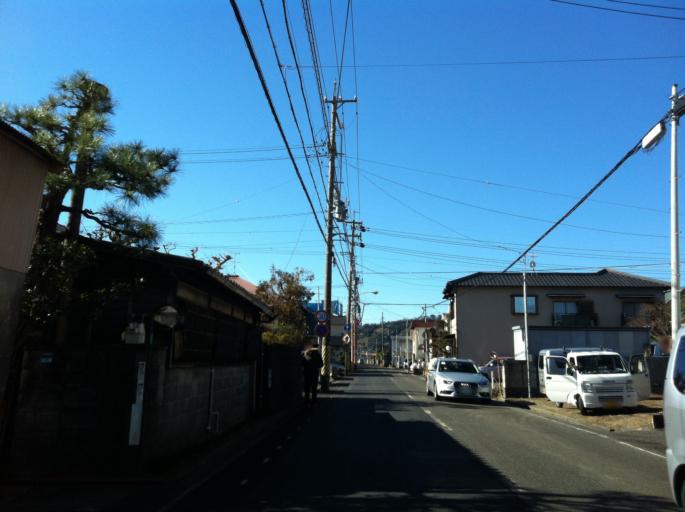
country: JP
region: Shizuoka
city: Shizuoka-shi
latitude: 34.9990
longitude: 138.3921
